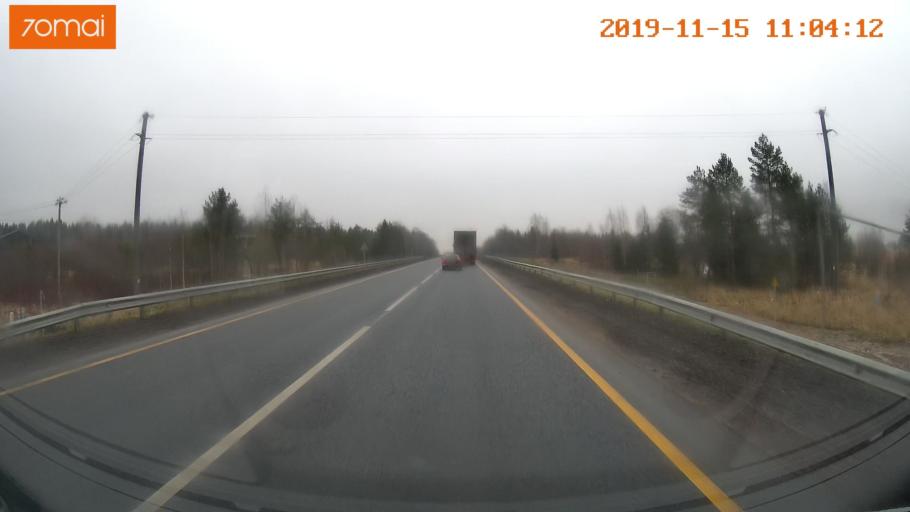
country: RU
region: Vologda
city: Chebsara
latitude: 59.1213
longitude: 38.9782
